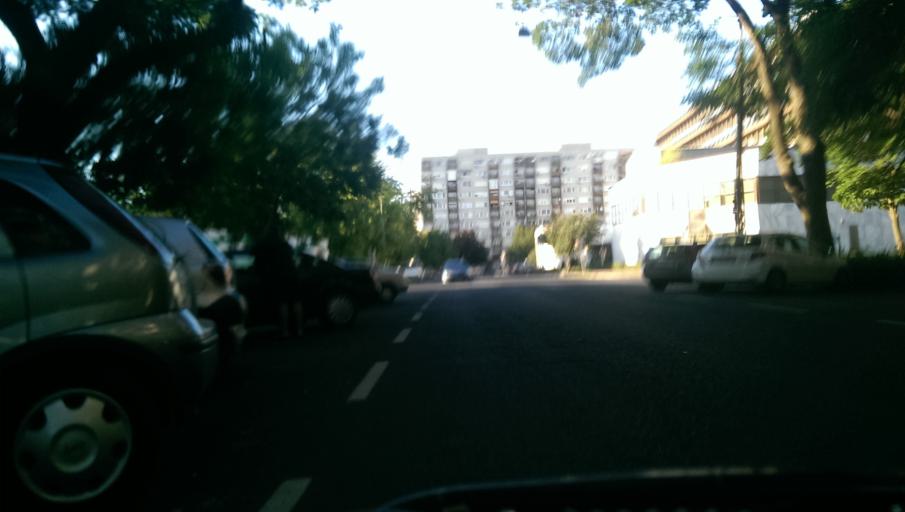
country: HU
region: Budapest
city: Budapest III. keruelet
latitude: 47.5220
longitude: 19.0536
